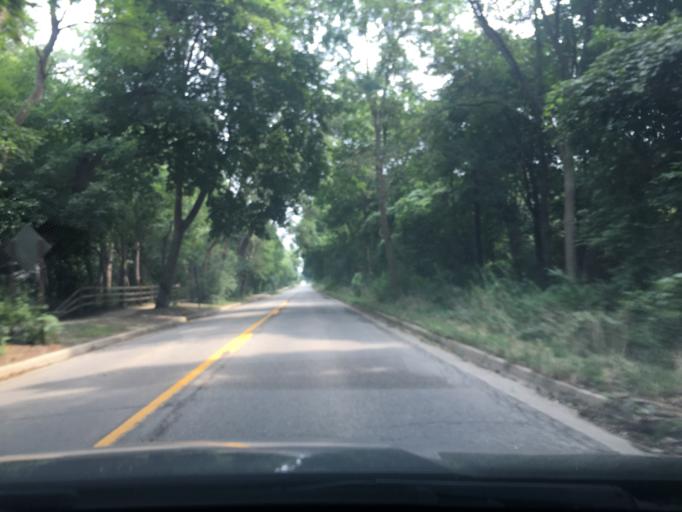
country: US
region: Michigan
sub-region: Oakland County
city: Birmingham
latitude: 42.5711
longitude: -83.2203
